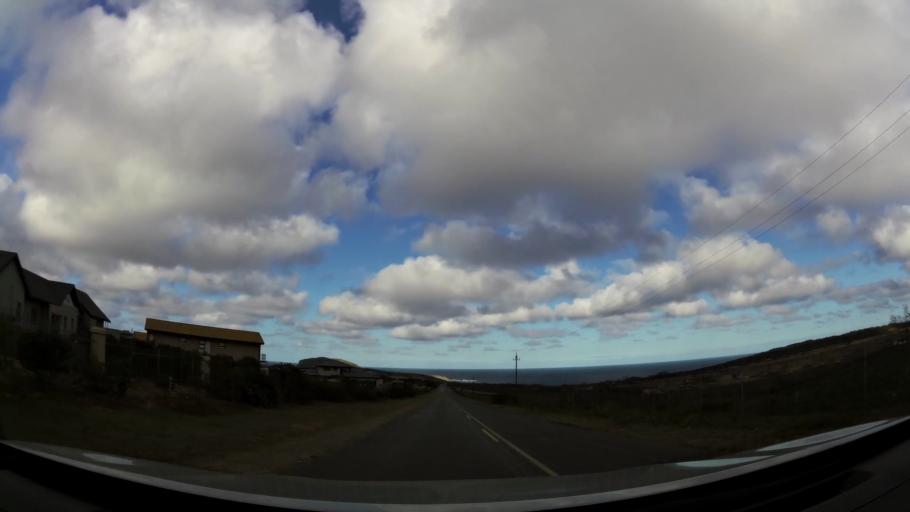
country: ZA
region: Western Cape
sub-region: Eden District Municipality
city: Plettenberg Bay
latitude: -34.0919
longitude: 23.3588
